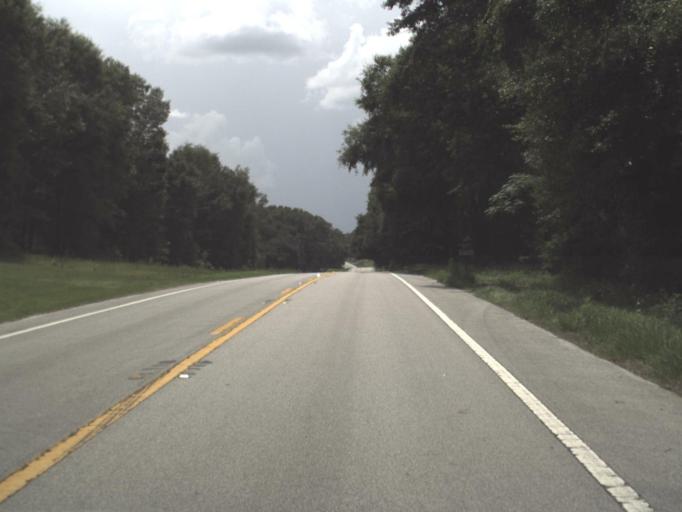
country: US
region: Florida
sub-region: Madison County
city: Madison
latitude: 30.4723
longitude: -83.3517
